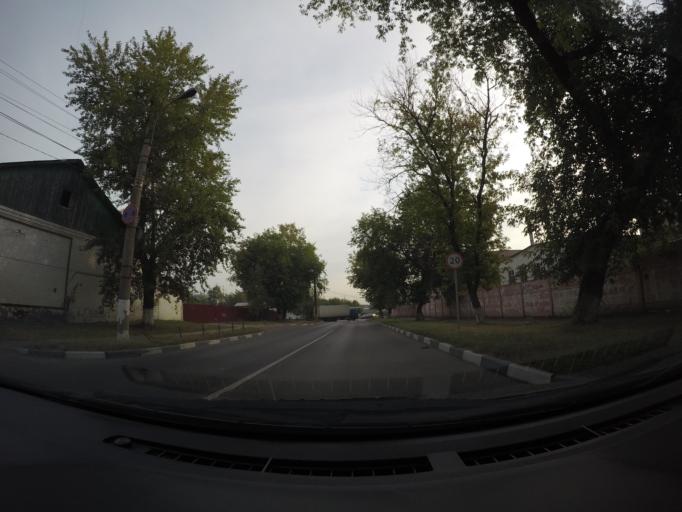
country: RU
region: Moskovskaya
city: Lyubertsy
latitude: 55.6713
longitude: 37.9129
